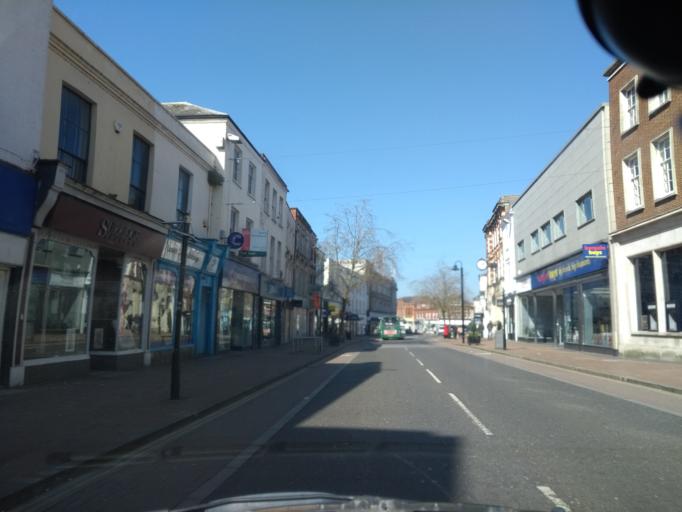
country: GB
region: England
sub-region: Somerset
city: Taunton
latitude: 51.0154
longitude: -3.1033
